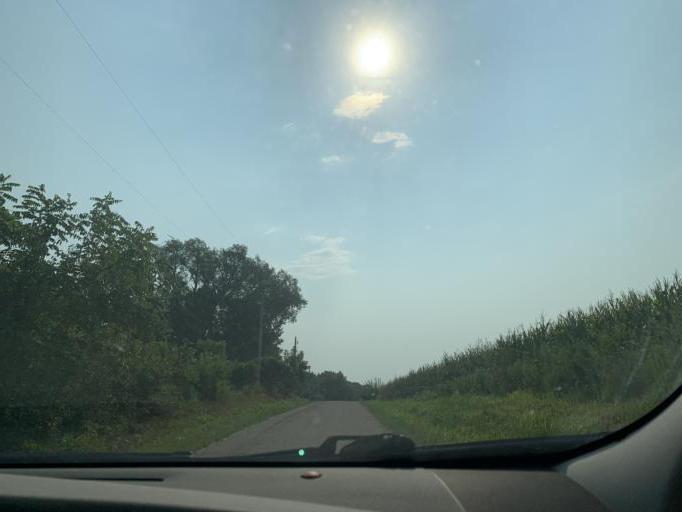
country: US
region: Illinois
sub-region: Whiteside County
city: Morrison
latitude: 41.8617
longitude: -89.8794
